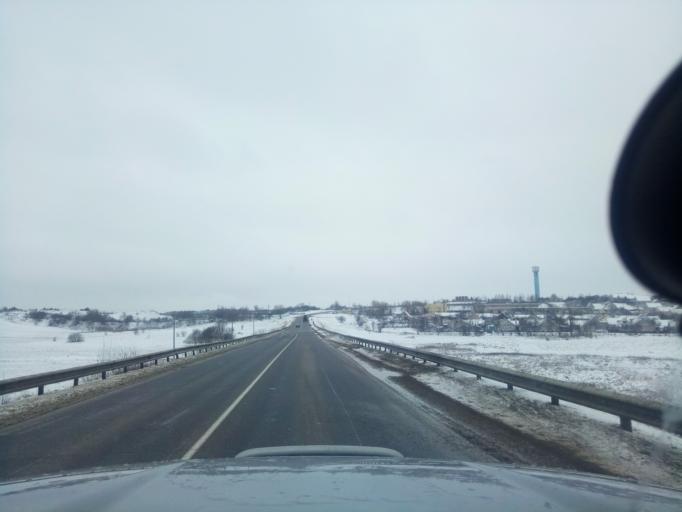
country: BY
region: Minsk
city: Kapyl'
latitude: 53.1434
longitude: 27.0801
